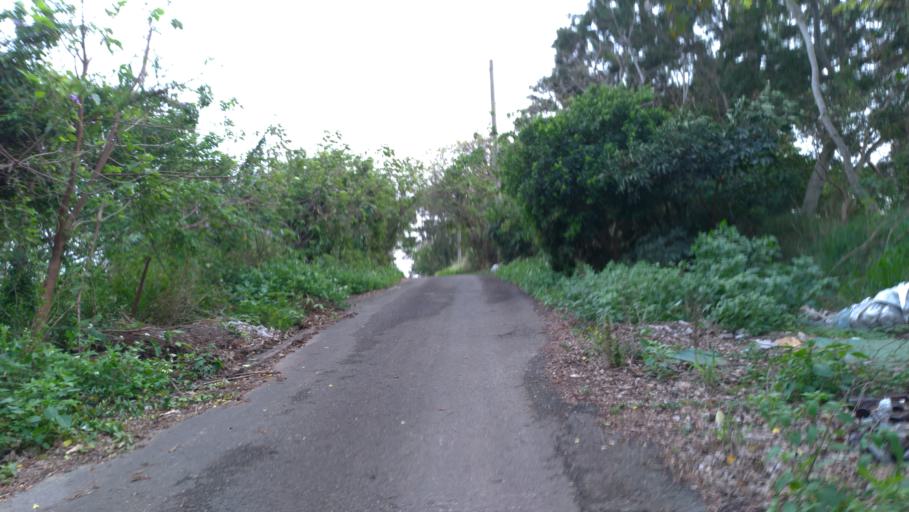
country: TW
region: Taiwan
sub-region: Hsinchu
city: Hsinchu
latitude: 24.7524
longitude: 120.9849
